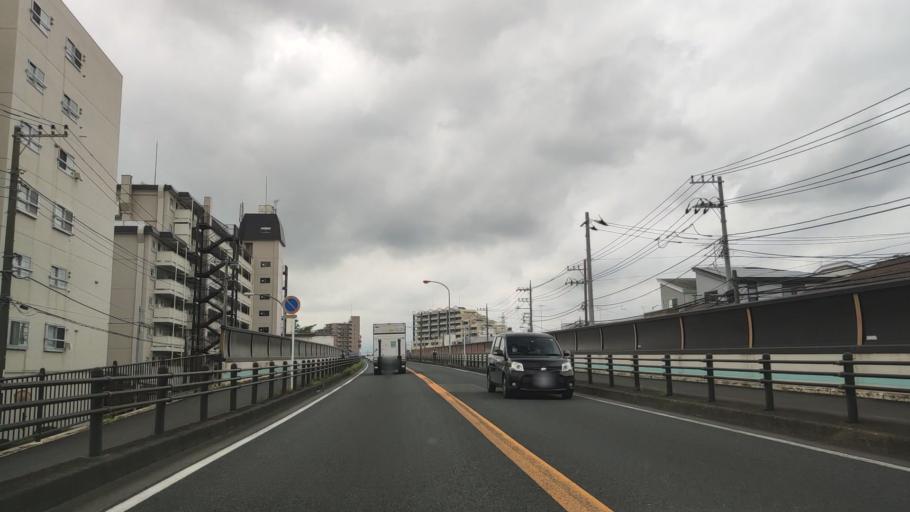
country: JP
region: Kanagawa
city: Minami-rinkan
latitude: 35.5013
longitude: 139.4476
